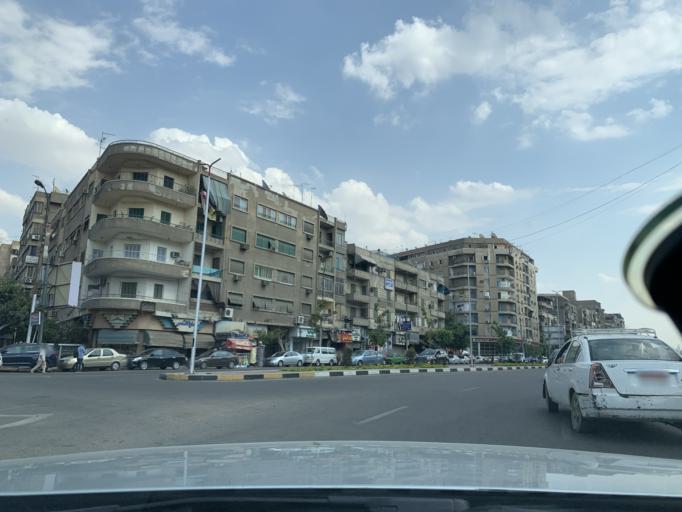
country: EG
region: Muhafazat al Qahirah
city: Cairo
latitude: 30.1052
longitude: 31.3437
